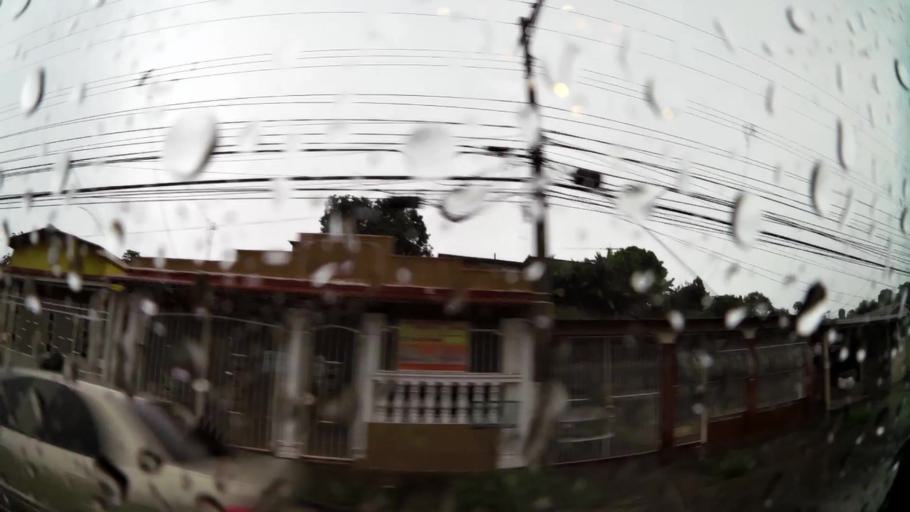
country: PA
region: Panama
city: San Miguelito
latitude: 9.0526
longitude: -79.4747
